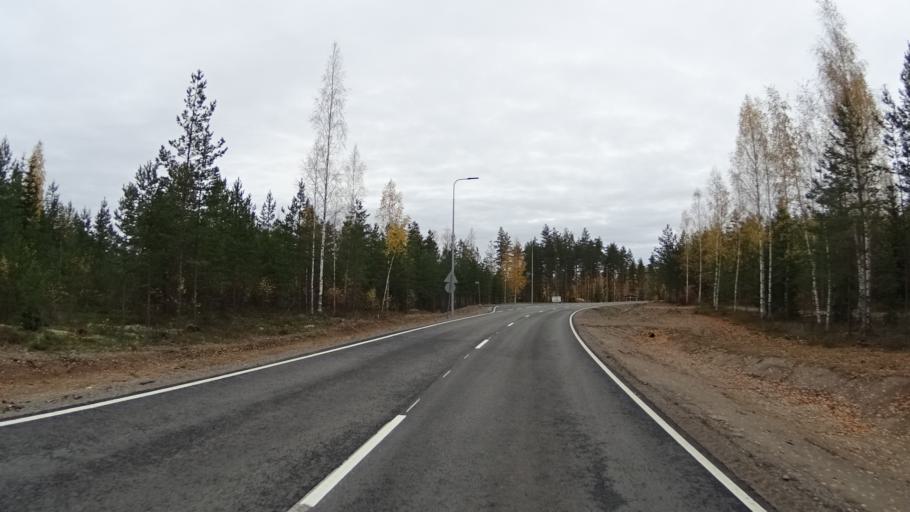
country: FI
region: South Karelia
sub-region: Lappeenranta
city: Luumaeki
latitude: 60.9313
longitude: 27.6309
